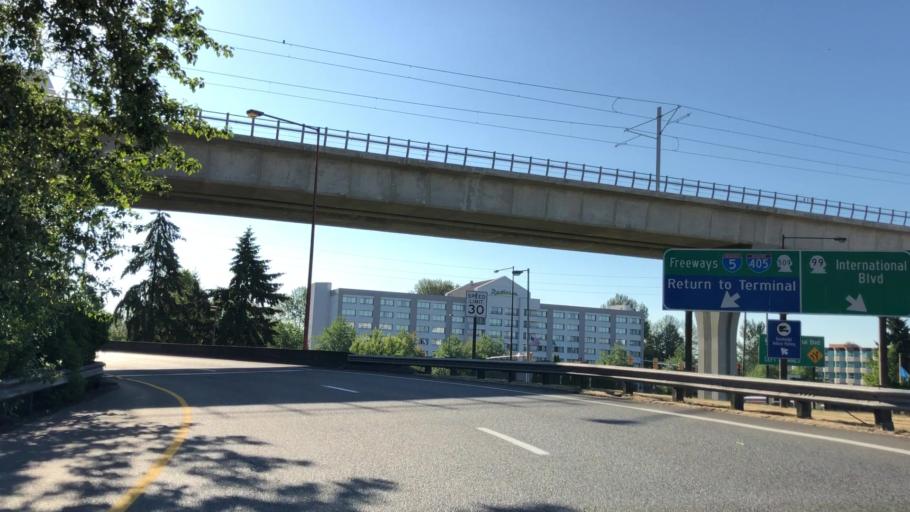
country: US
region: Washington
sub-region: King County
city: SeaTac
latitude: 47.4408
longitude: -122.2982
